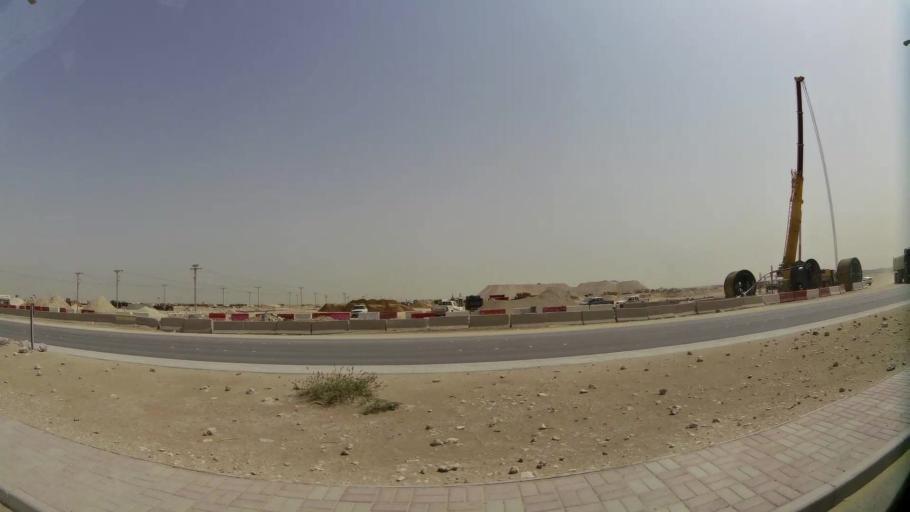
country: QA
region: Baladiyat ar Rayyan
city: Ar Rayyan
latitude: 25.1748
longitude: 51.3994
